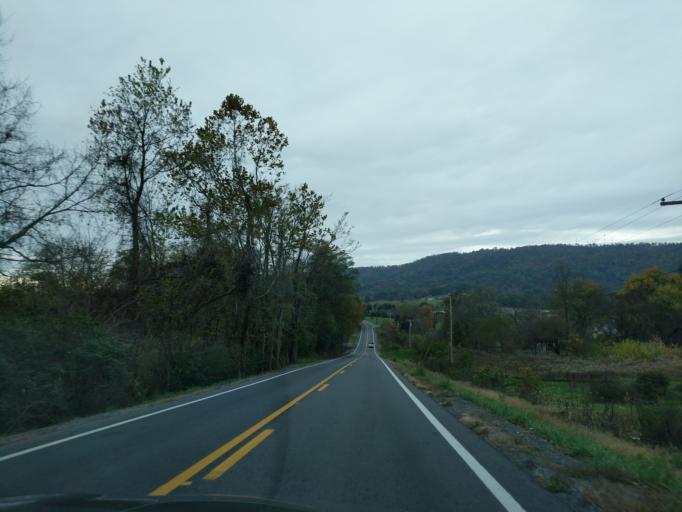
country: US
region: West Virginia
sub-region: Berkeley County
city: Inwood
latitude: 39.4124
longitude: -78.0614
